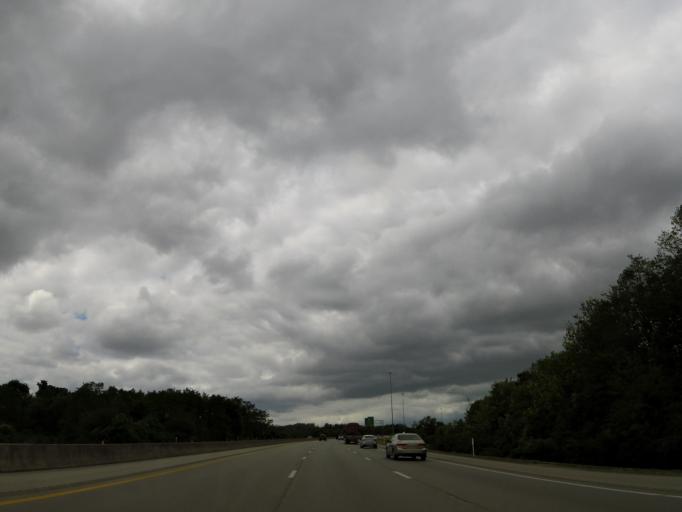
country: US
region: Kentucky
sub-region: Fayette County
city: Lexington
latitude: 37.9522
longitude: -84.3872
